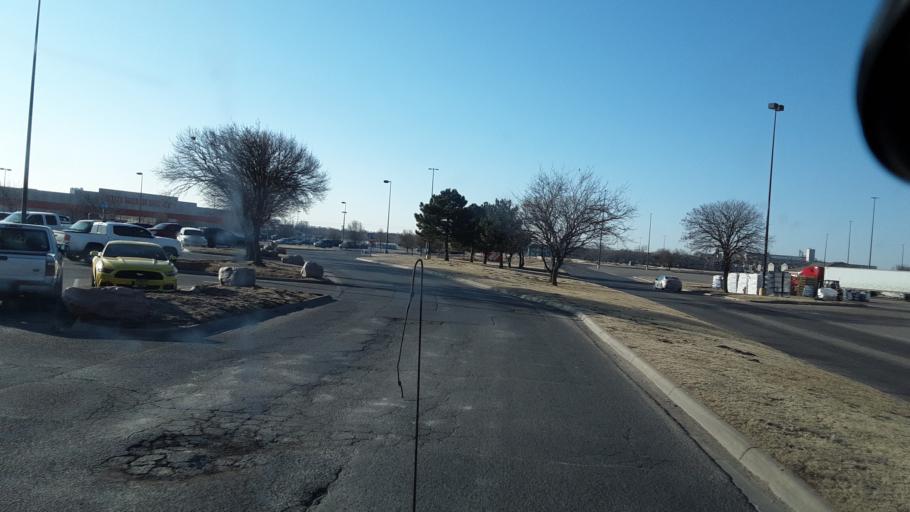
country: US
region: Kansas
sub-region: Reno County
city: Hutchinson
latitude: 38.0699
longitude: -97.8946
